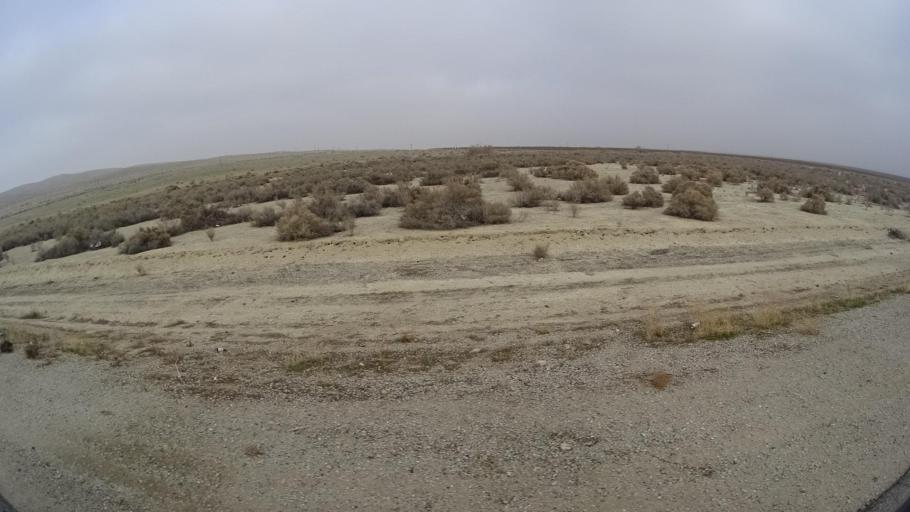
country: US
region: California
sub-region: Kern County
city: Maricopa
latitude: 35.1262
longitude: -119.3640
